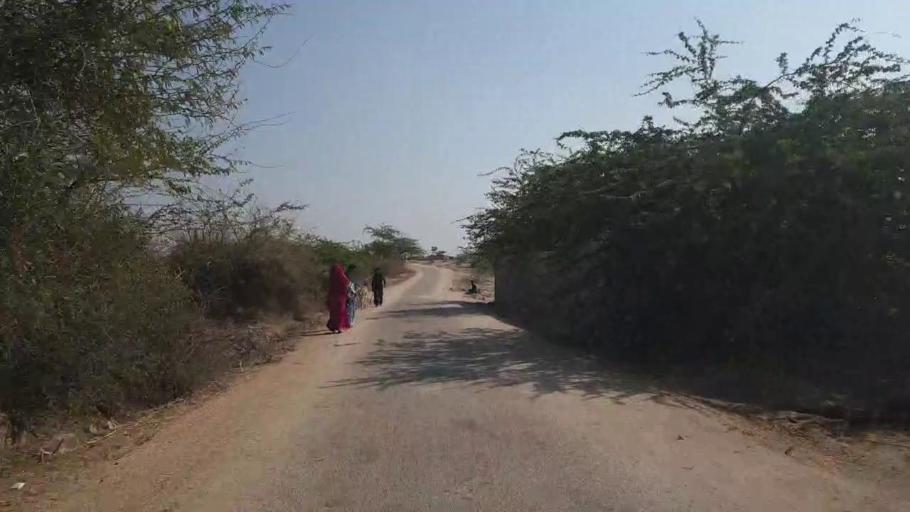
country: PK
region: Sindh
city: Dhoro Naro
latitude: 25.5020
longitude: 69.6302
